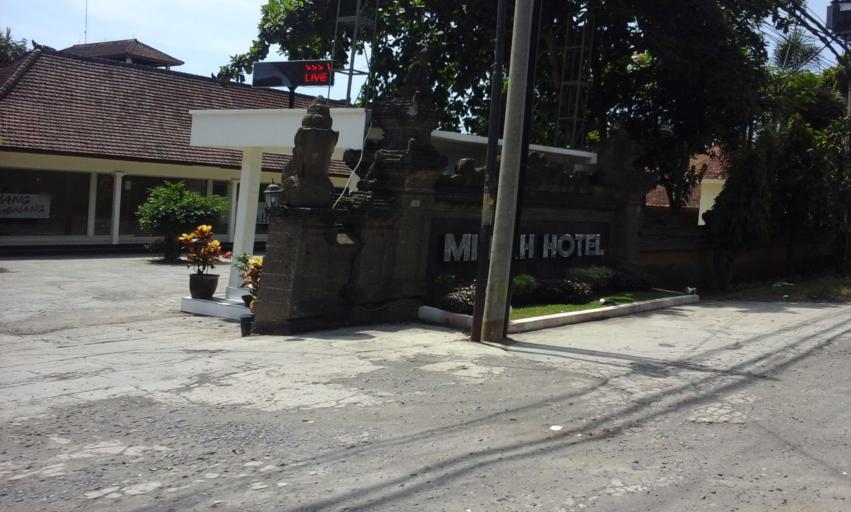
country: ID
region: East Java
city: Klatakan
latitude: -8.1725
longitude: 114.3855
